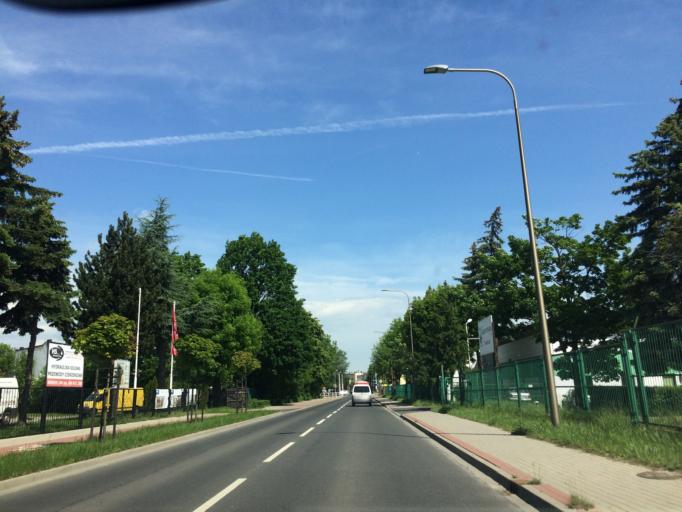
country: PL
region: Lower Silesian Voivodeship
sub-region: Powiat swidnicki
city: Swidnica
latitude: 50.8313
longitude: 16.5001
